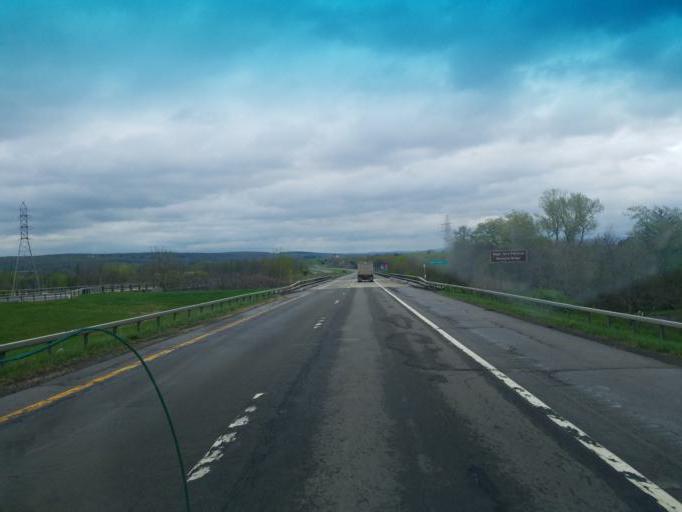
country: US
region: New York
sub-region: Chautauqua County
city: Falconer
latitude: 42.1253
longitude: -79.2062
